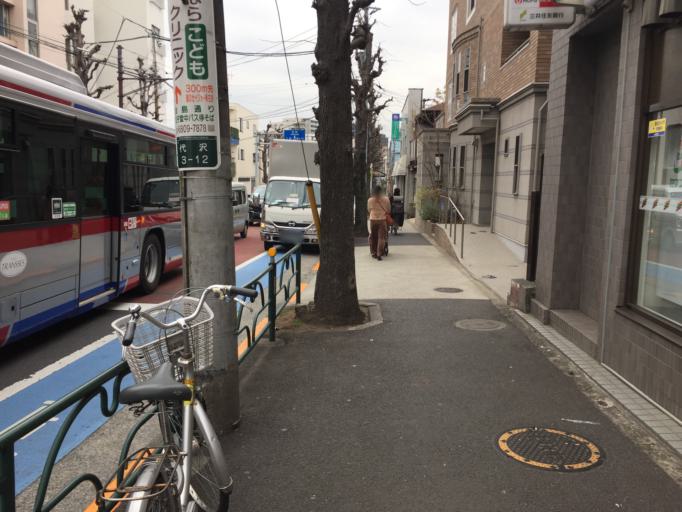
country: JP
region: Tokyo
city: Tokyo
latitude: 35.6547
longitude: 139.6734
